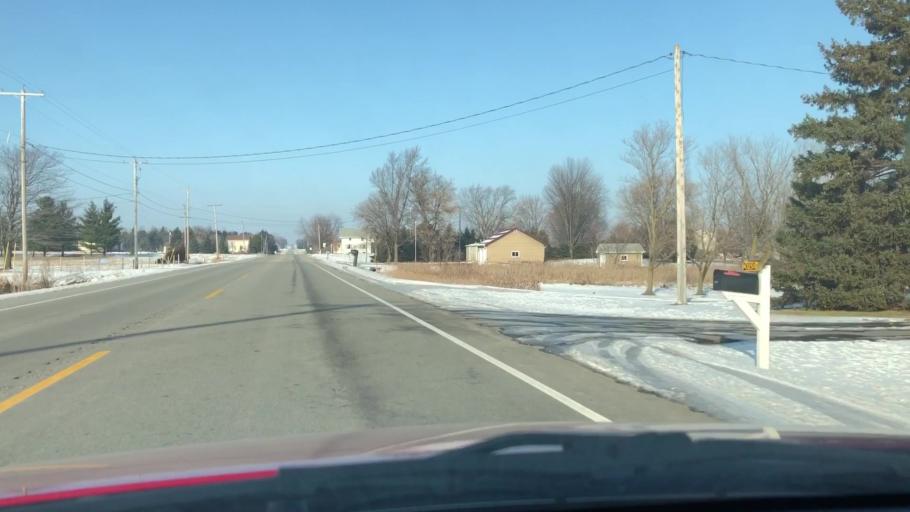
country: US
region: Wisconsin
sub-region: Outagamie County
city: Kimberly
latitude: 44.3561
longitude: -88.3749
